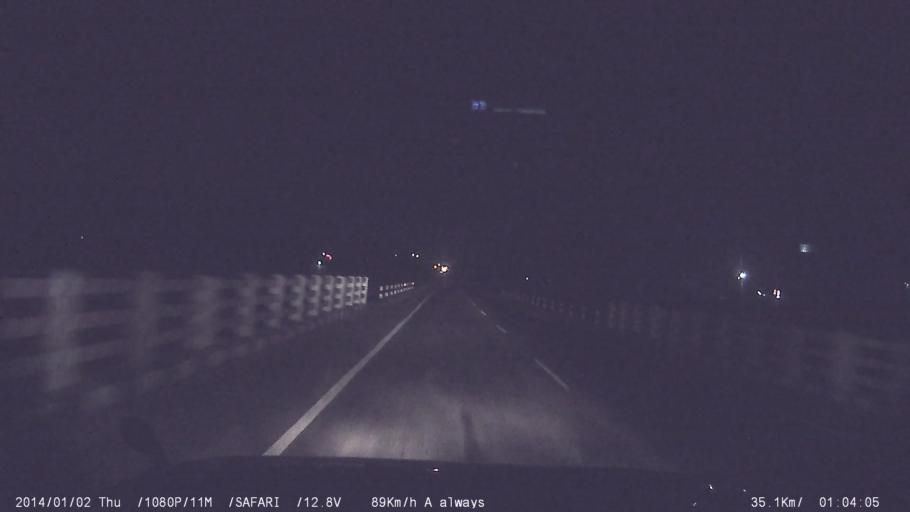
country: IN
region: Tamil Nadu
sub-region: Coimbatore
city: Madukkarai
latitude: 10.9077
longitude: 76.9763
